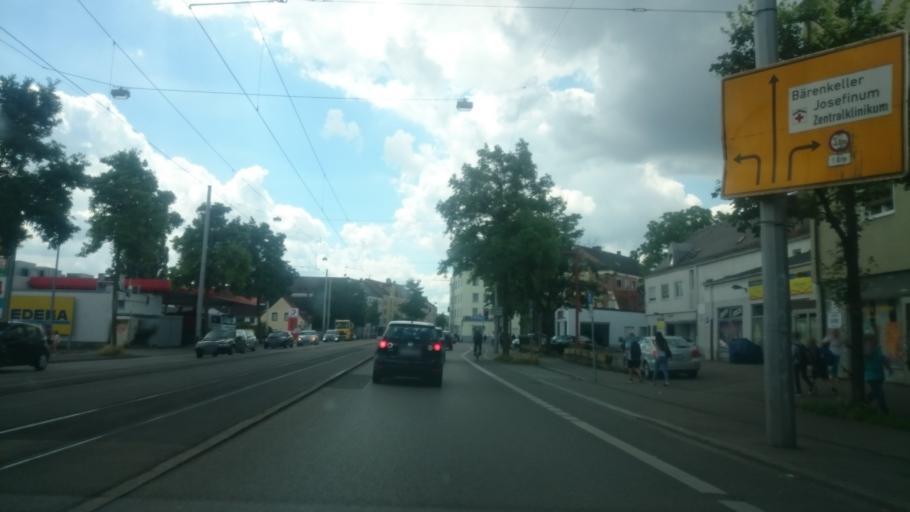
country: DE
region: Bavaria
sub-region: Swabia
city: Augsburg
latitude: 48.3900
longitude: 10.8814
